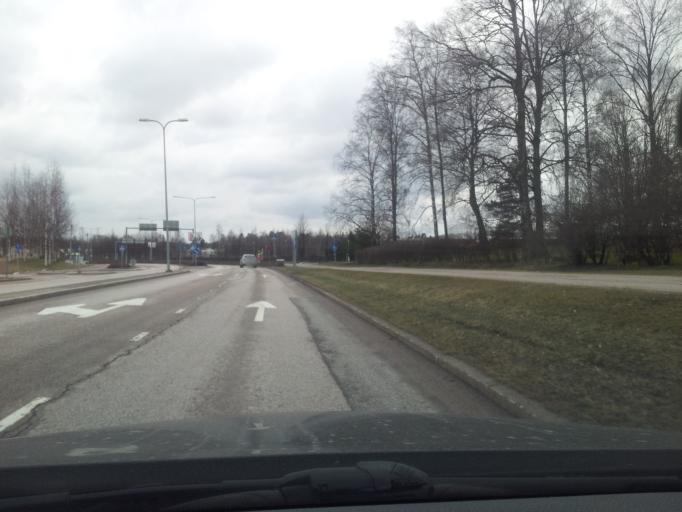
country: FI
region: Uusimaa
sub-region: Helsinki
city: Koukkuniemi
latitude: 60.1802
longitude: 24.7793
